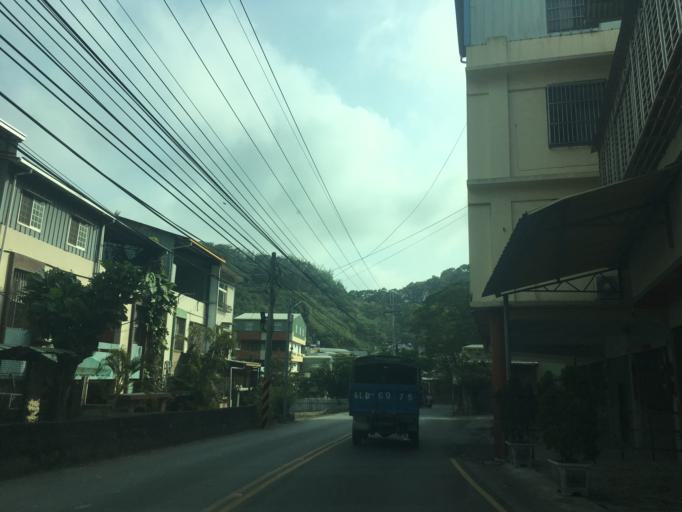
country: TW
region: Taiwan
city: Fengyuan
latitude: 24.2361
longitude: 120.7390
